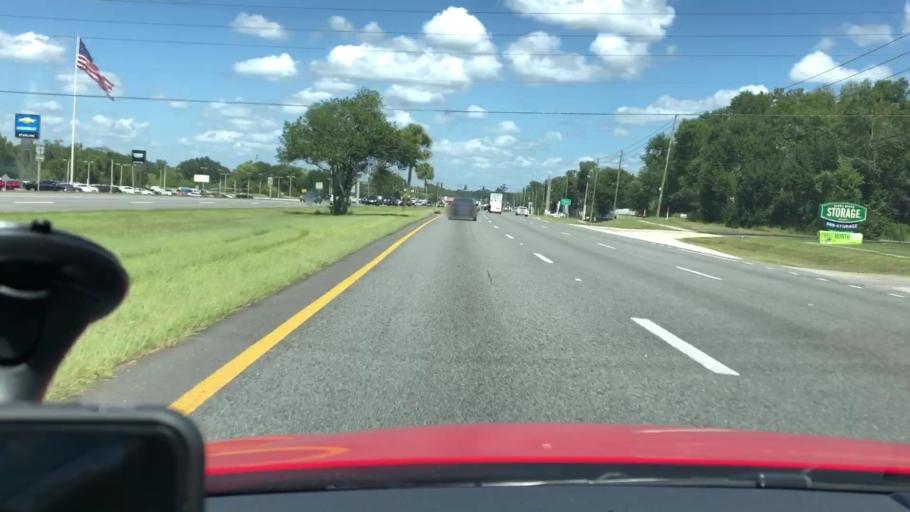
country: US
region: Florida
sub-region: Volusia County
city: Orange City
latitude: 28.9787
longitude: -81.2993
